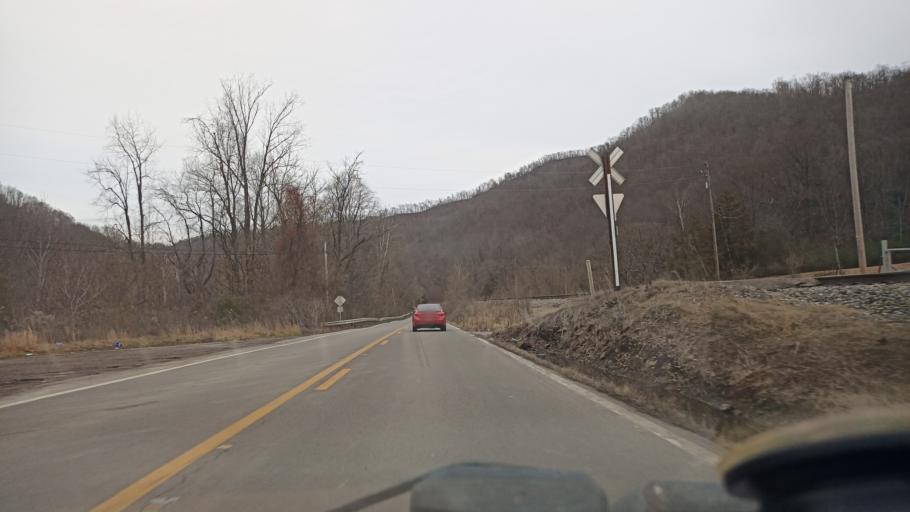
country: US
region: West Virginia
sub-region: Logan County
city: Mallory
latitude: 37.6967
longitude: -81.8708
